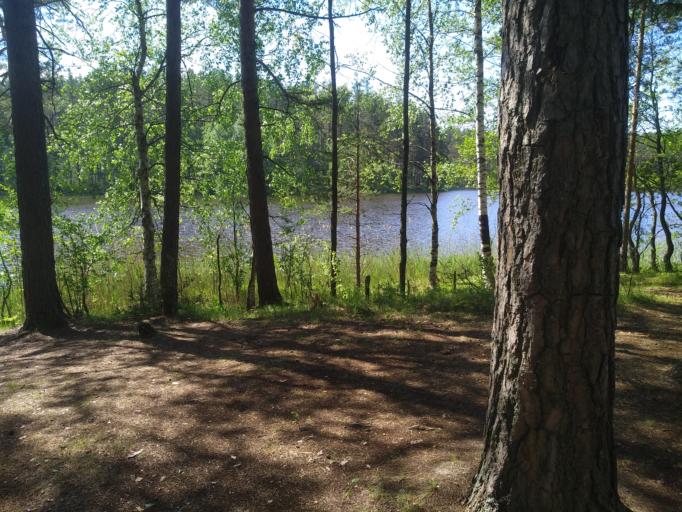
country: RU
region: Leningrad
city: Michurinskoye
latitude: 60.6024
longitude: 29.8608
